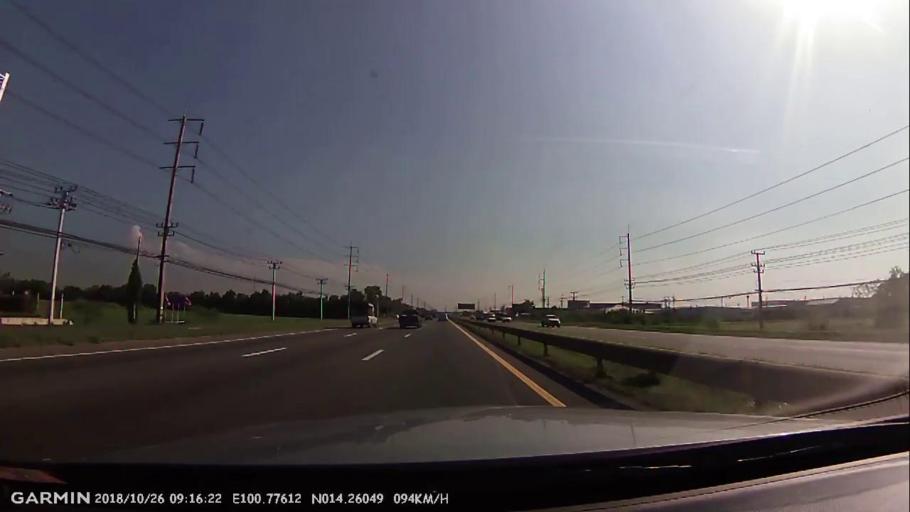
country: TH
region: Phra Nakhon Si Ayutthaya
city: Wang Noi
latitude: 14.2609
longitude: 100.7760
